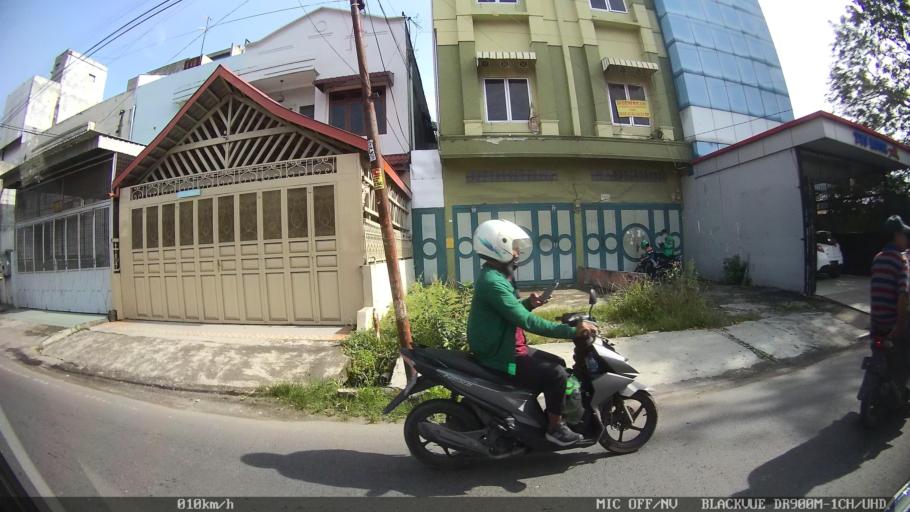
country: ID
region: North Sumatra
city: Medan
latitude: 3.6040
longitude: 98.6541
